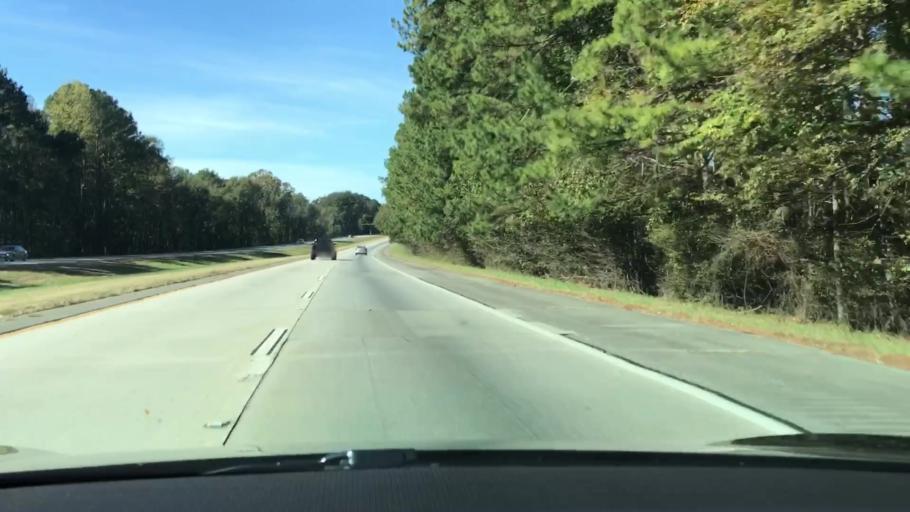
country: US
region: Georgia
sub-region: Taliaferro County
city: Crawfordville
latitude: 33.5281
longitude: -82.9500
